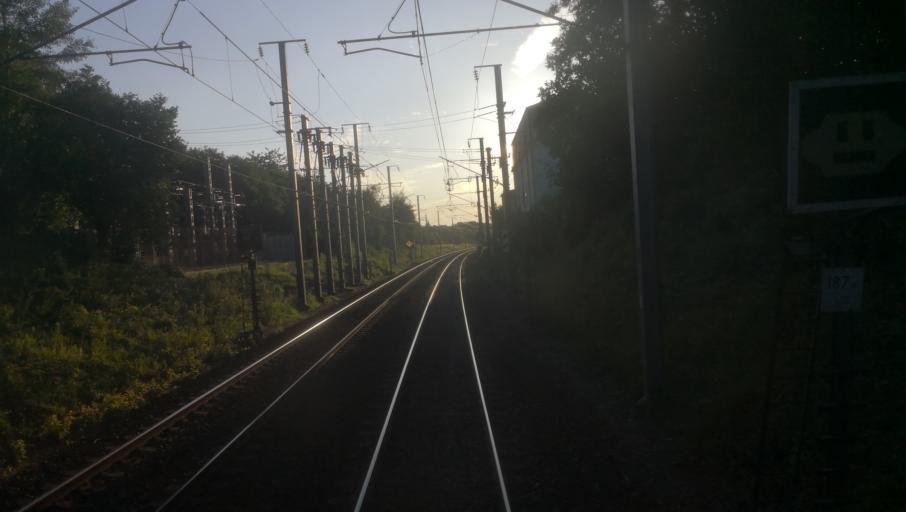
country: FR
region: Lower Normandy
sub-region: Departement du Calvados
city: Beuvillers
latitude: 49.1270
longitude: 0.2617
